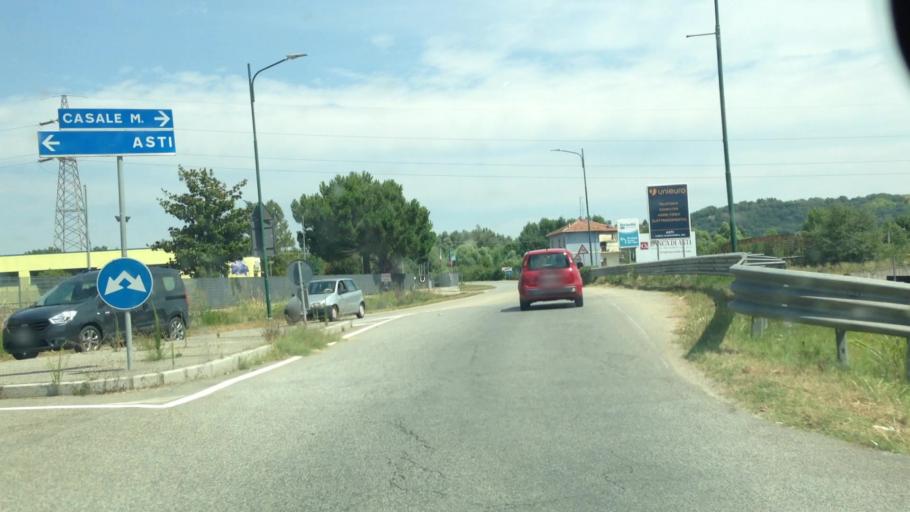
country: IT
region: Piedmont
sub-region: Provincia di Asti
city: Asti
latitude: 44.9198
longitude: 8.2257
